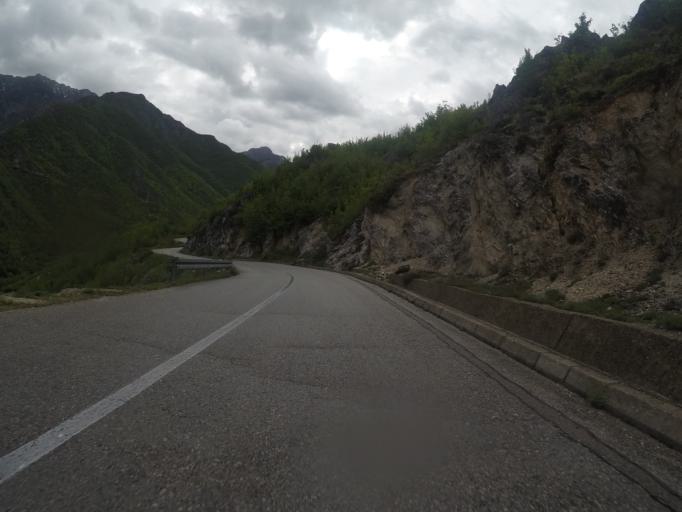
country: BA
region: Federation of Bosnia and Herzegovina
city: Siroki Brijeg
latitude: 43.5392
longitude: 17.6194
